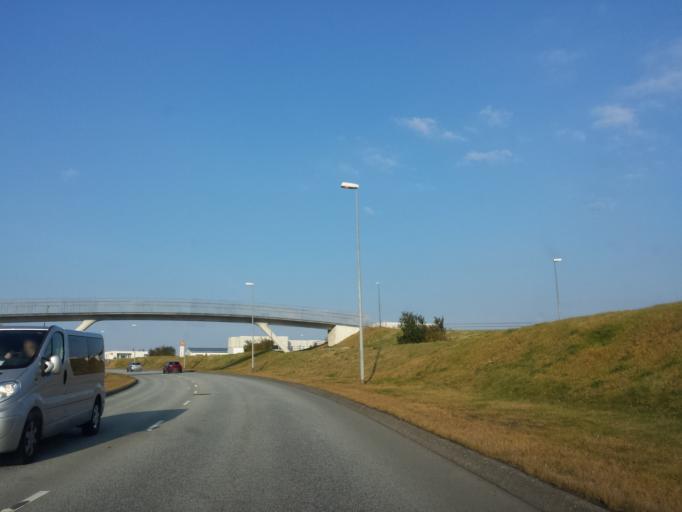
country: IS
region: Capital Region
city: Reykjavik
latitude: 64.0892
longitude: -21.8075
